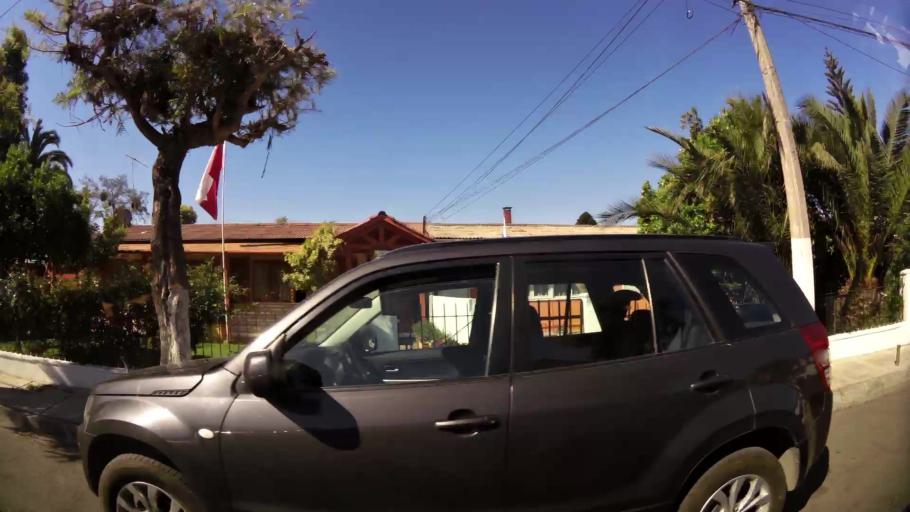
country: CL
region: Santiago Metropolitan
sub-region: Provincia de Talagante
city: Penaflor
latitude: -33.6040
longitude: -70.8995
